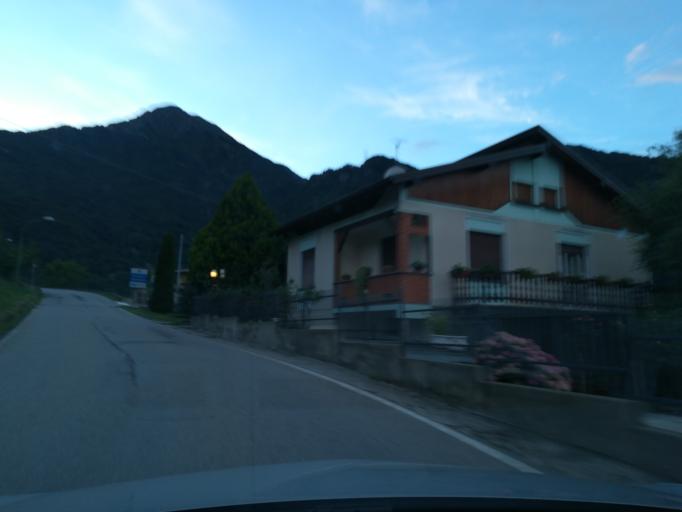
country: IT
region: Lombardy
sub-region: Provincia di Bergamo
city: Valsecca
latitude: 45.8282
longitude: 9.4958
